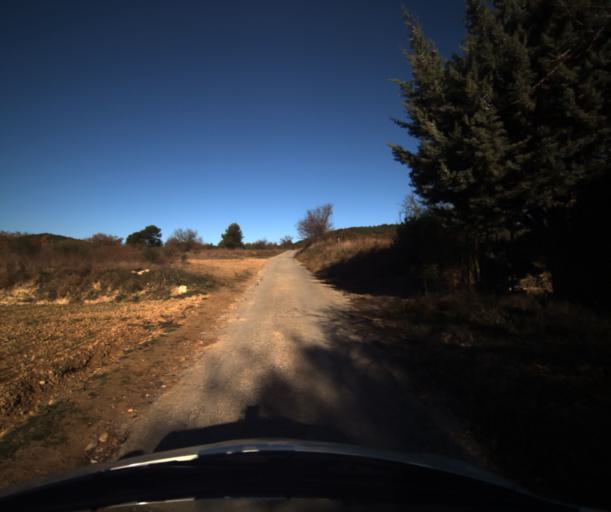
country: FR
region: Provence-Alpes-Cote d'Azur
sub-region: Departement du Vaucluse
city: Pertuis
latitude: 43.7090
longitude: 5.4991
